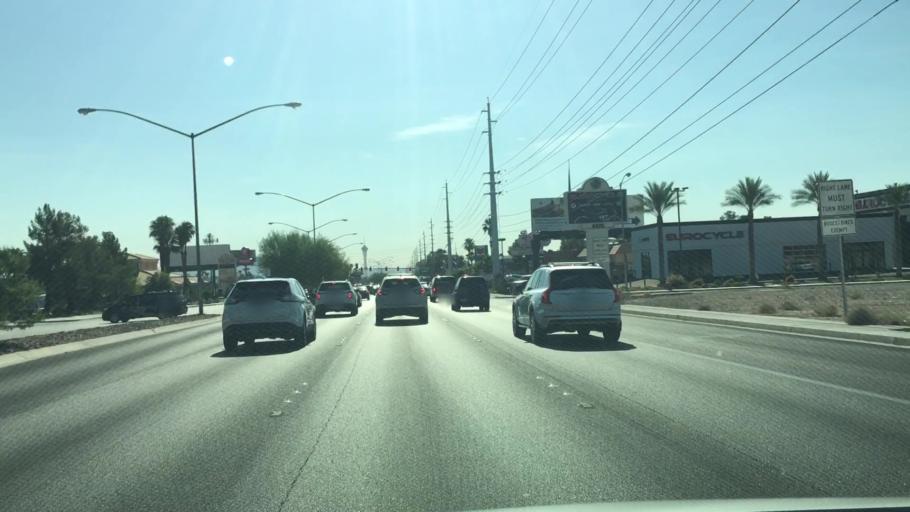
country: US
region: Nevada
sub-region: Clark County
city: Spring Valley
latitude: 36.1441
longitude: -115.2281
